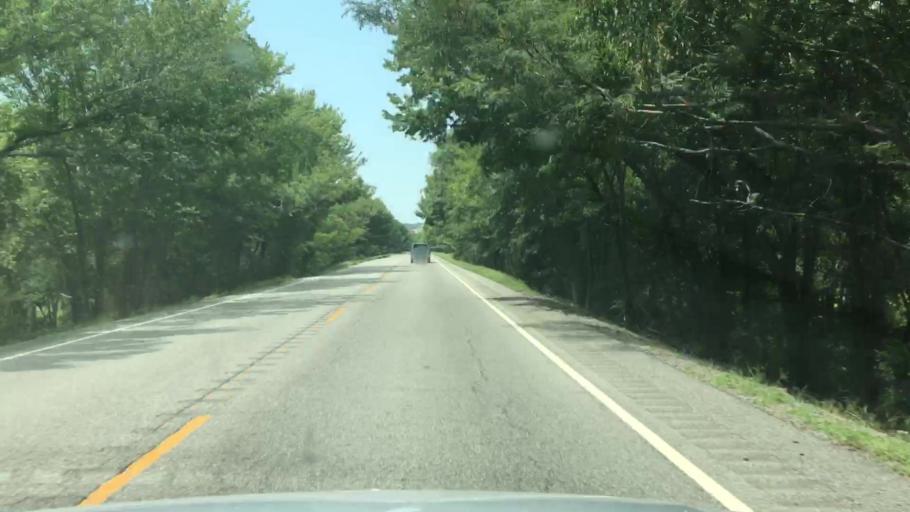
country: US
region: Oklahoma
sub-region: Muskogee County
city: Fort Gibson
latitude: 35.9369
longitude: -95.2163
